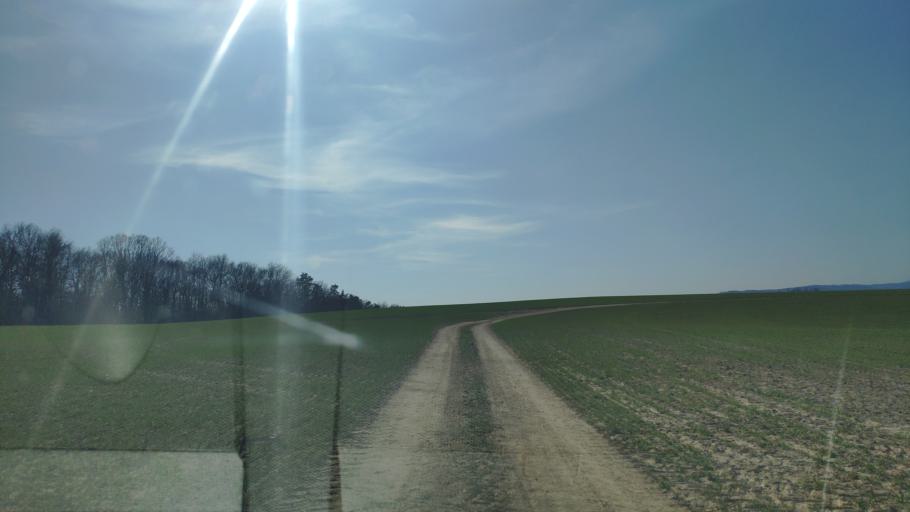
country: SK
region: Banskobystricky
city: Revuca
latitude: 48.5454
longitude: 20.2770
